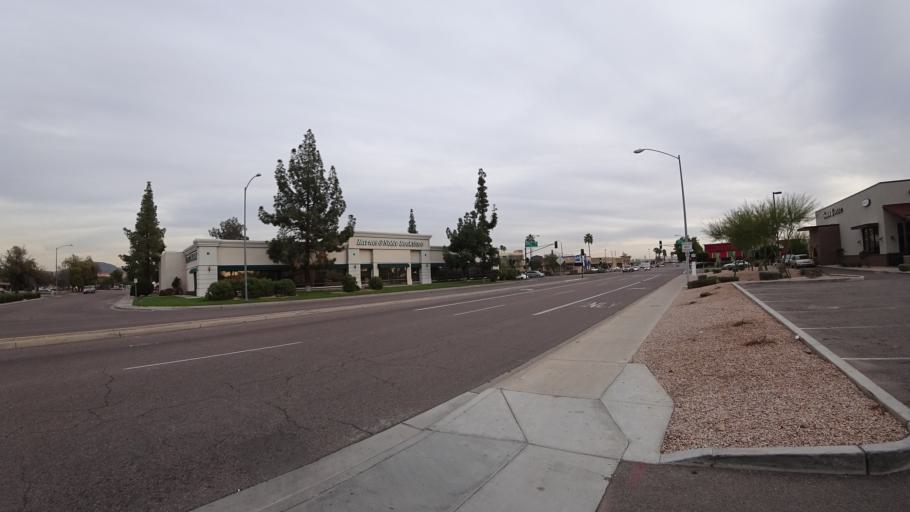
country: US
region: Arizona
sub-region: Maricopa County
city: Glendale
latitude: 33.5810
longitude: -112.1222
